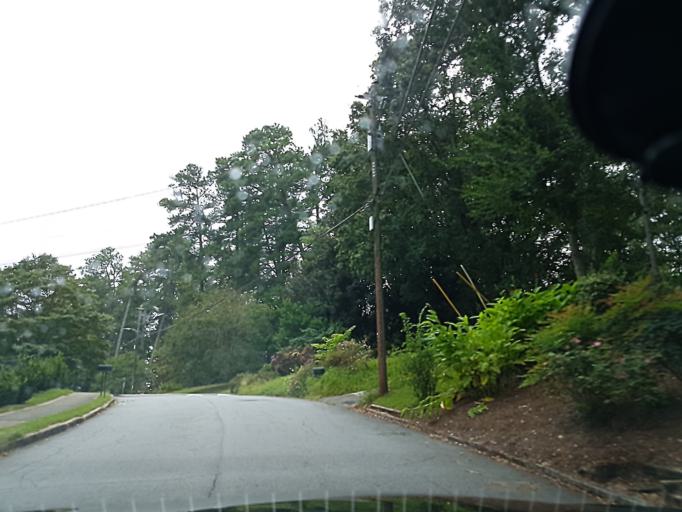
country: US
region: Georgia
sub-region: DeKalb County
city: North Druid Hills
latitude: 33.8177
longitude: -84.3178
